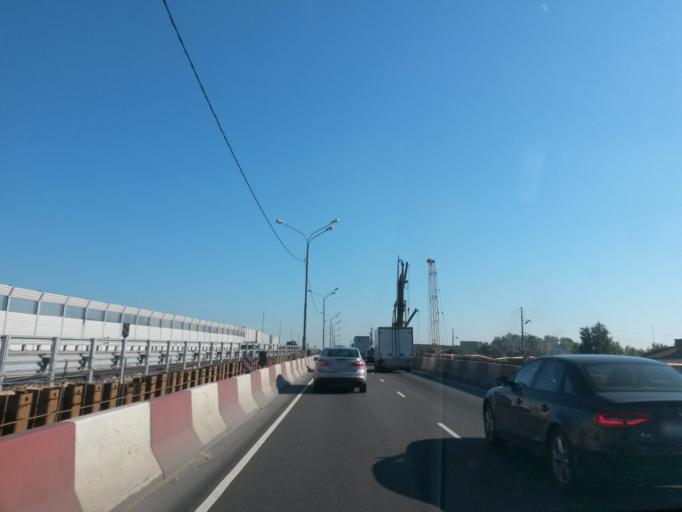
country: RU
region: Moskovskaya
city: Korolev
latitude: 55.9237
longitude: 37.7982
